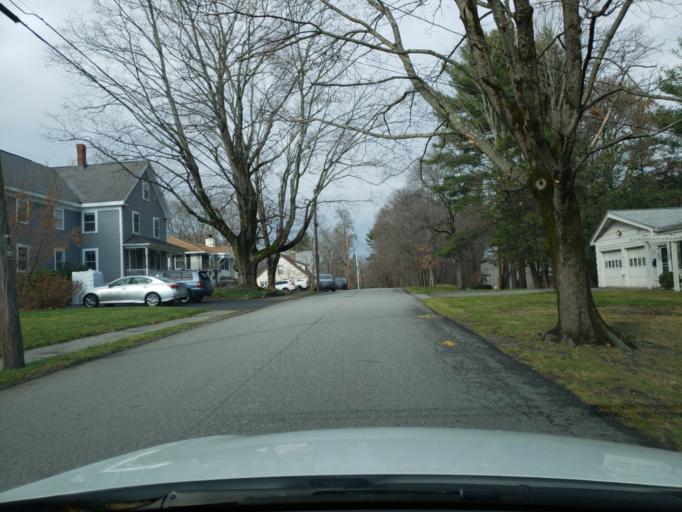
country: US
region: Massachusetts
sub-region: Essex County
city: Andover
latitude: 42.6618
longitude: -71.1313
